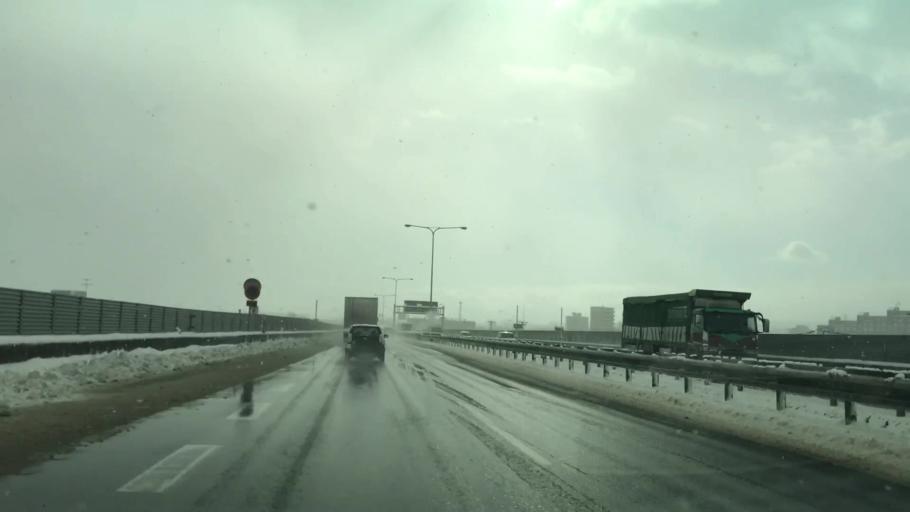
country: JP
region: Hokkaido
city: Sapporo
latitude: 43.0570
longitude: 141.4269
